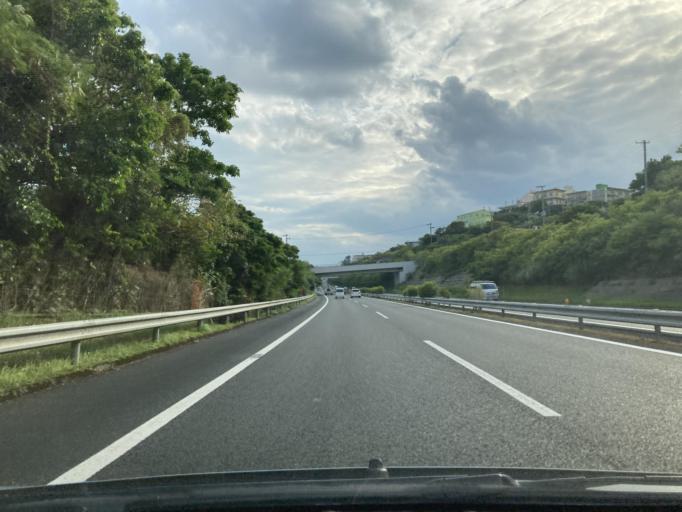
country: JP
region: Okinawa
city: Ginowan
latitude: 26.2696
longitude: 127.7759
